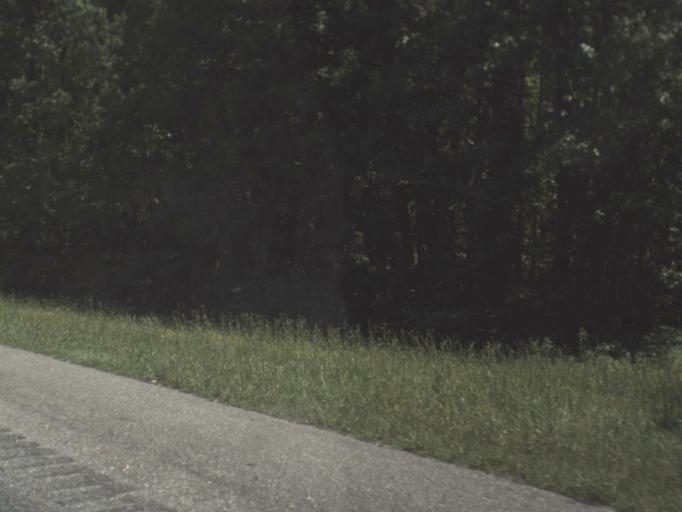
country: US
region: Florida
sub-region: Jefferson County
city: Monticello
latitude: 30.4874
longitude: -83.9600
